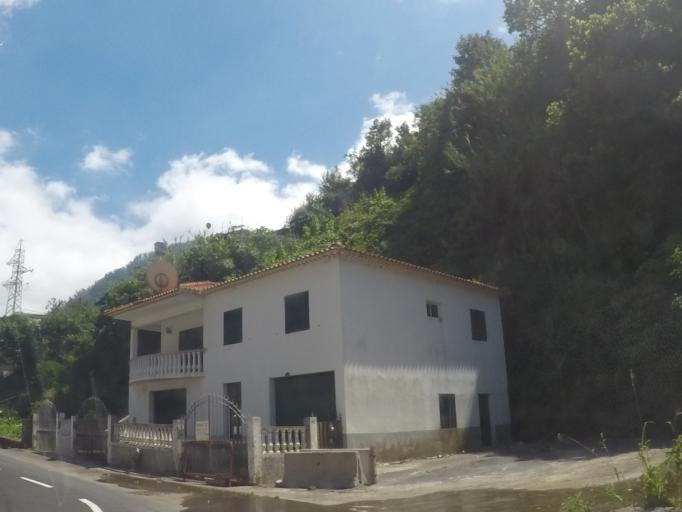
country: PT
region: Madeira
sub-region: Camara de Lobos
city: Curral das Freiras
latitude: 32.7137
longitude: -16.9711
